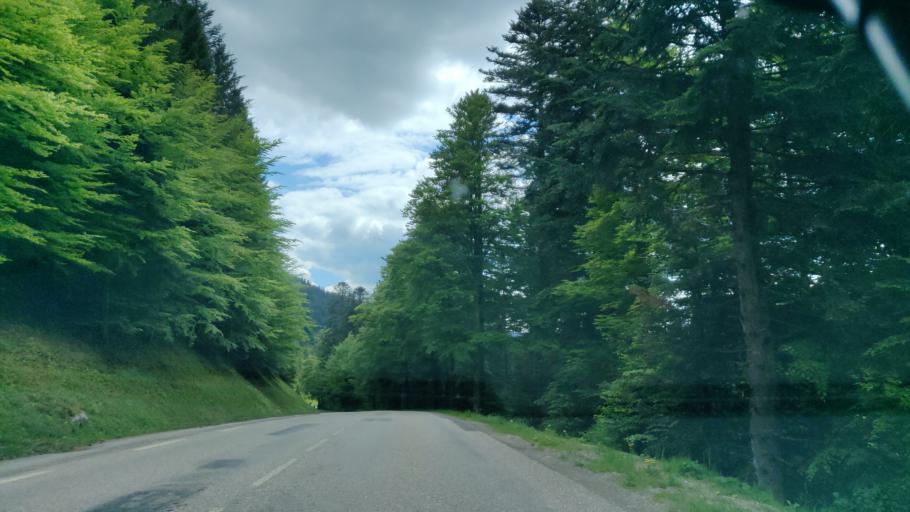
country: FR
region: Lorraine
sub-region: Departement des Vosges
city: Xonrupt-Longemer
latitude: 48.0310
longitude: 6.9624
